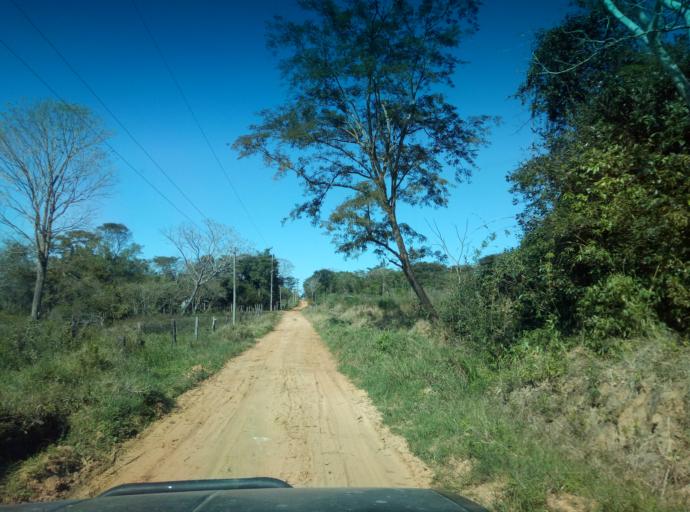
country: PY
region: Caaguazu
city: Doctor Cecilio Baez
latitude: -25.1749
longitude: -56.2020
